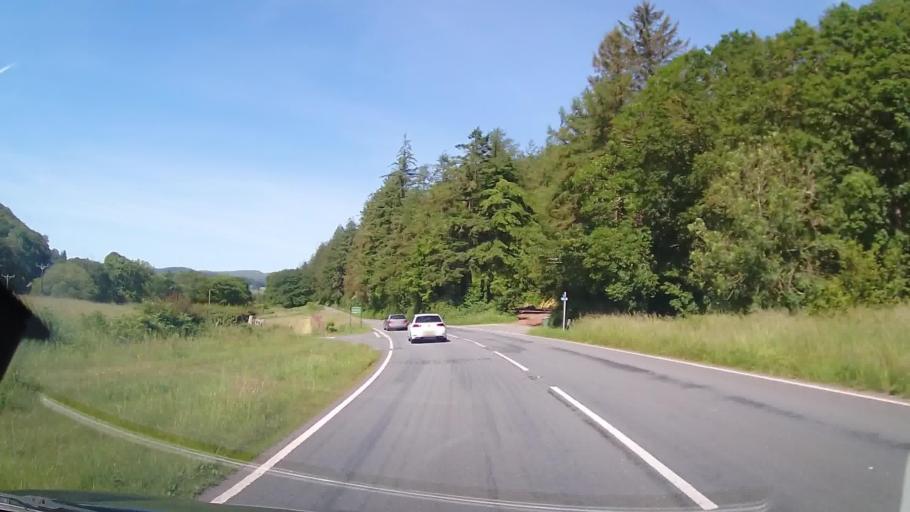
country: GB
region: Wales
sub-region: Sir Powys
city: Machynlleth
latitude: 52.5882
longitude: -3.8952
